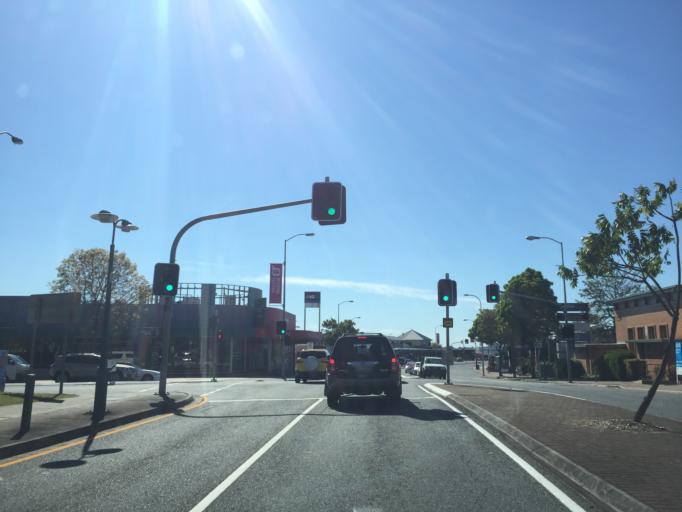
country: AU
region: Queensland
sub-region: Brisbane
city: Milton
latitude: -27.4457
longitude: 152.9918
